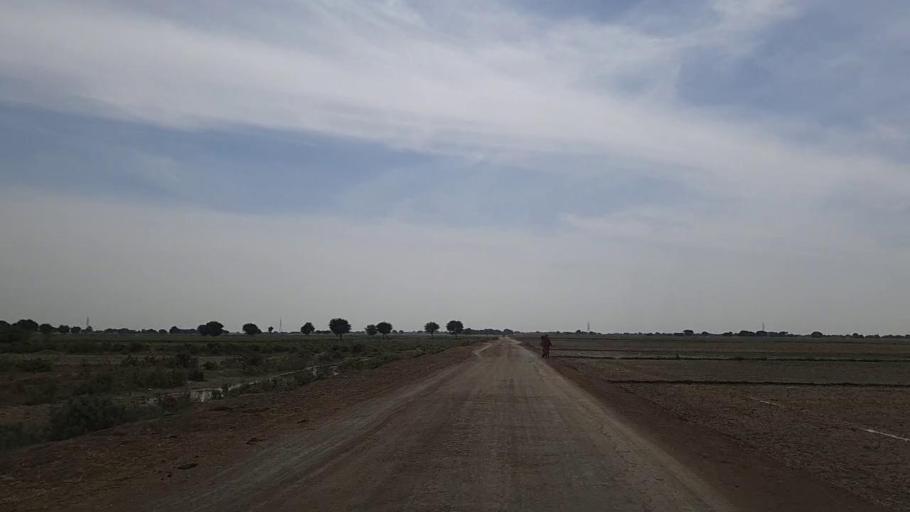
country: PK
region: Sindh
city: Samaro
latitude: 25.3031
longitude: 69.4529
